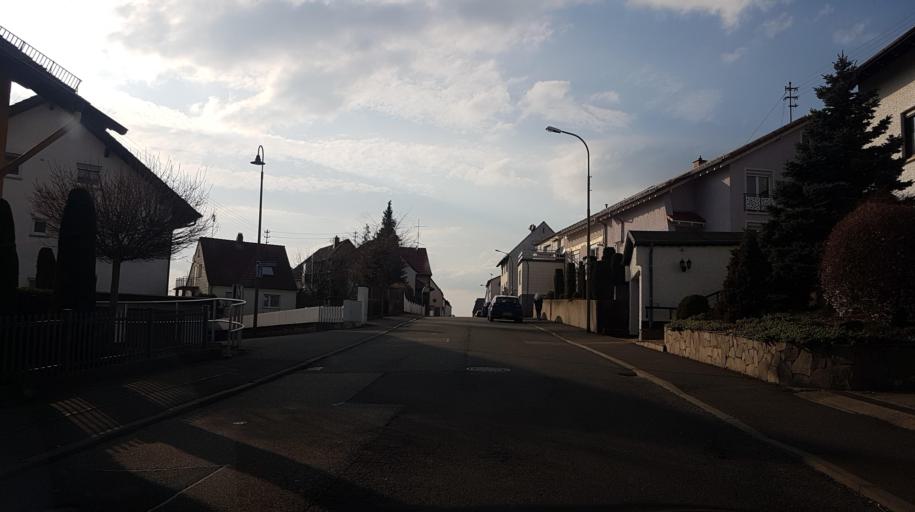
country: DE
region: Rheinland-Pfalz
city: Petersberg
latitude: 49.2263
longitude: 7.5864
